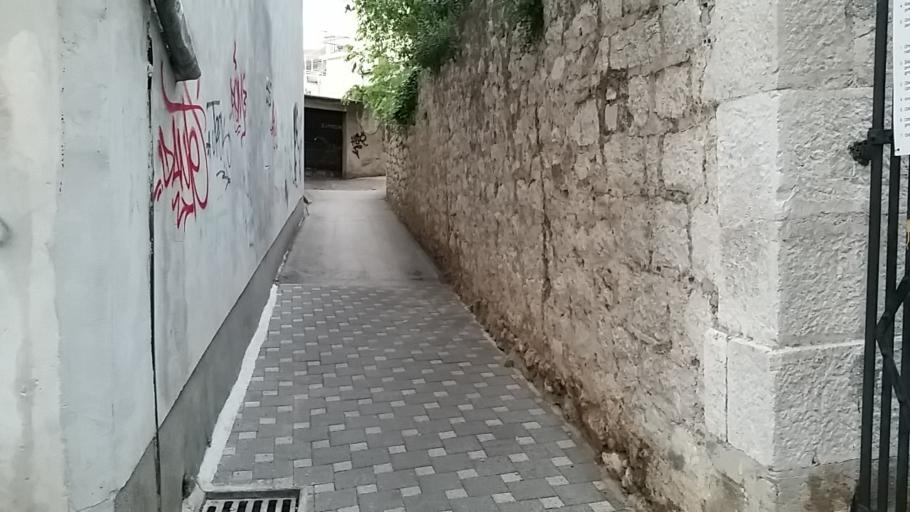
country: HR
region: Sibensko-Kniniska
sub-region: Grad Sibenik
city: Sibenik
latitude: 43.7352
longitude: 15.8959
